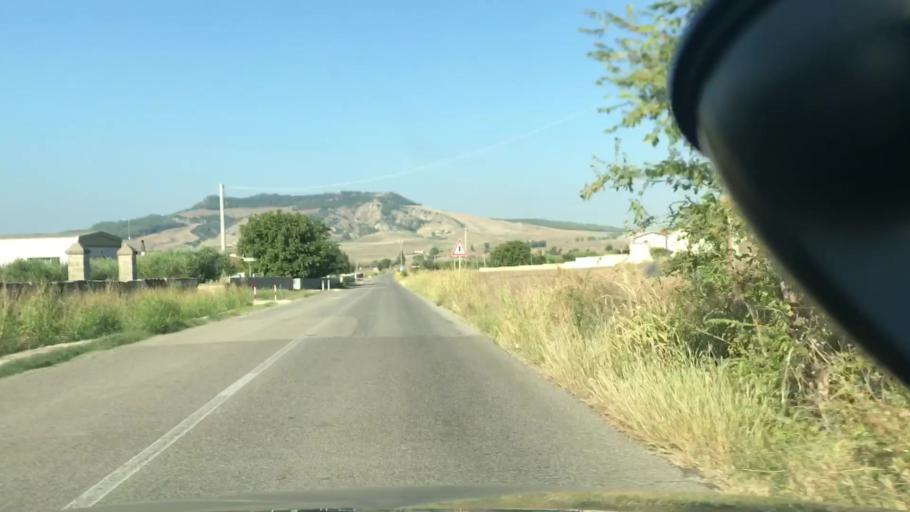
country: IT
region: Basilicate
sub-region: Provincia di Matera
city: La Martella
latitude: 40.6585
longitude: 16.5342
